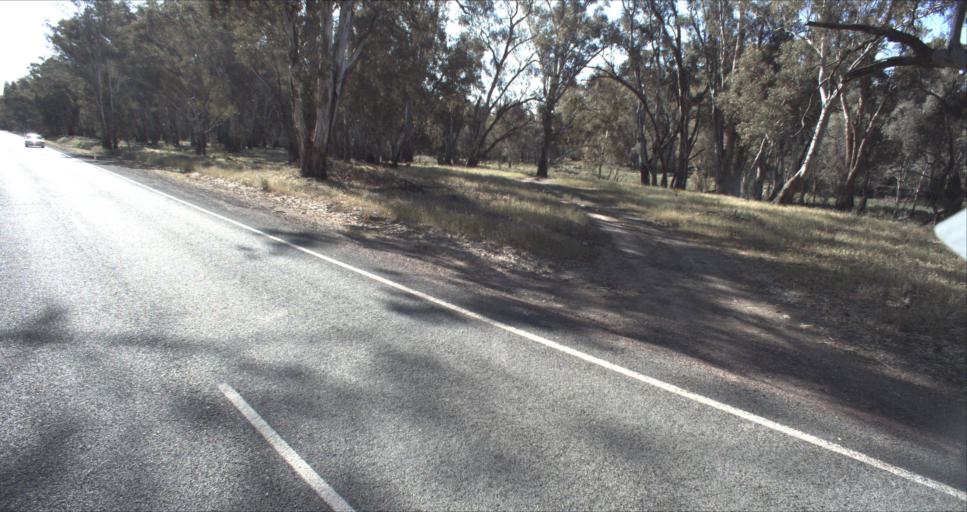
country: AU
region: New South Wales
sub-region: Leeton
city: Leeton
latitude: -34.6412
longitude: 146.3662
